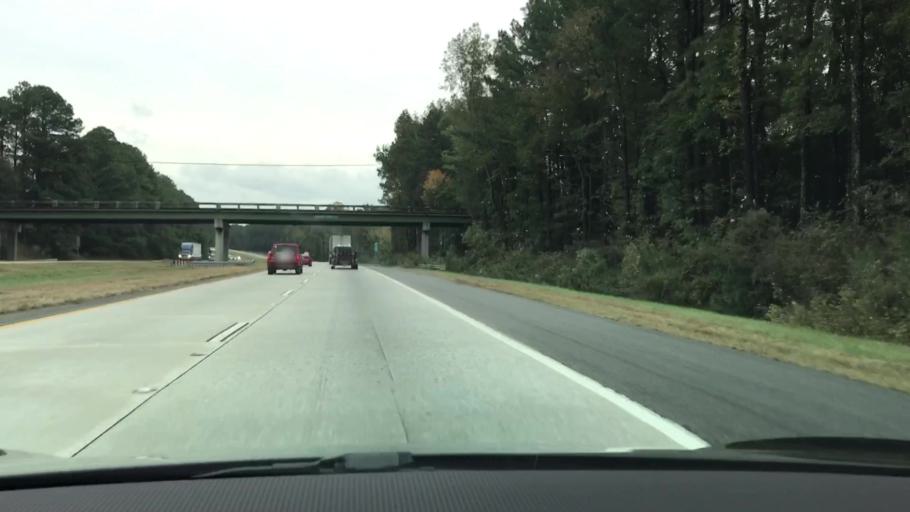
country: US
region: Georgia
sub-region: Taliaferro County
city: Crawfordville
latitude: 33.5279
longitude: -82.9583
